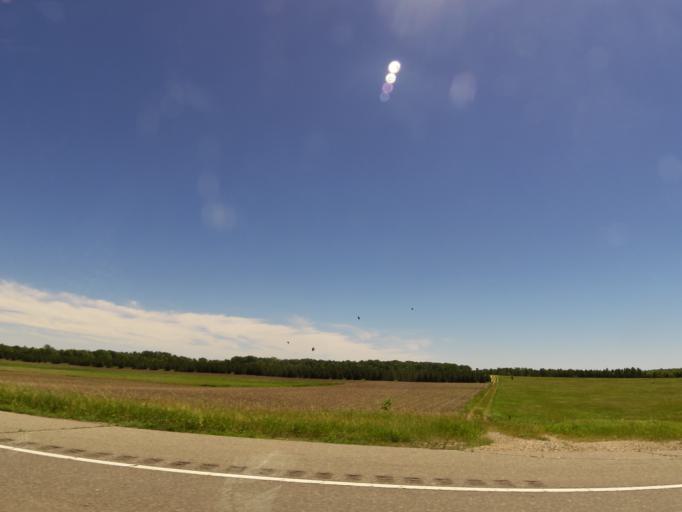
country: US
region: Minnesota
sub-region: Otter Tail County
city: Perham
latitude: 46.5517
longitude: -95.4820
